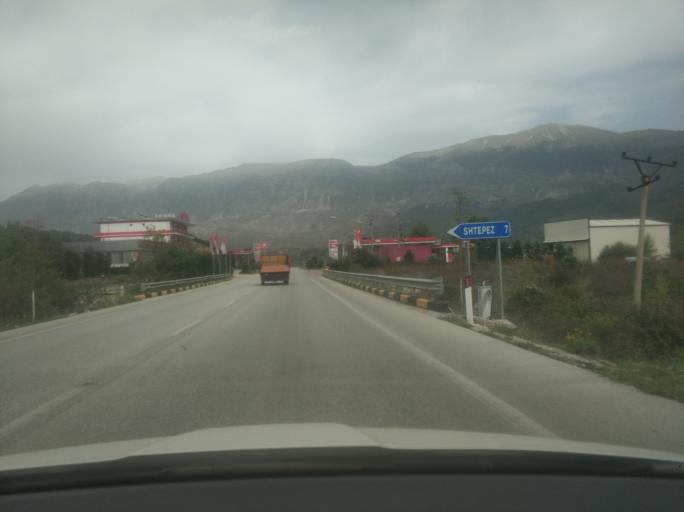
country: AL
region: Gjirokaster
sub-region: Rrethi i Gjirokastres
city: Picar
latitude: 40.1864
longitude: 20.0784
